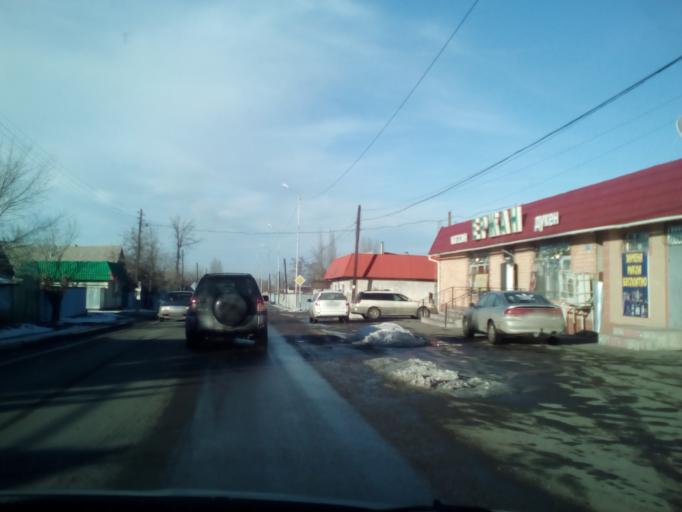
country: KZ
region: Almaty Oblysy
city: Burunday
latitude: 43.1723
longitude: 76.4157
